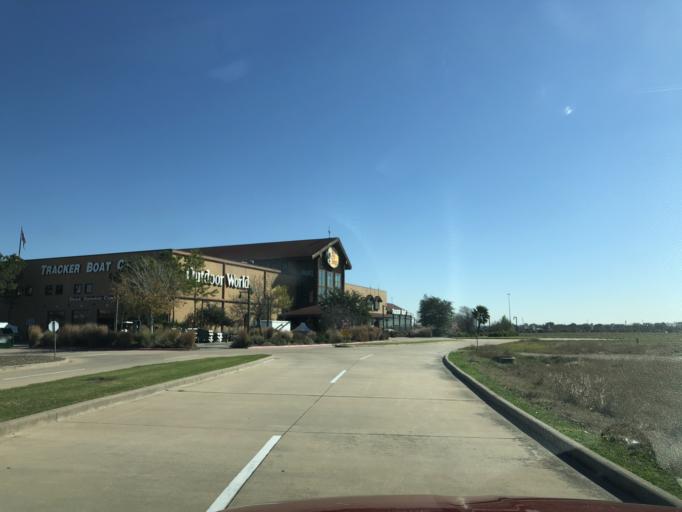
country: US
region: Texas
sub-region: Brazoria County
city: Brookside Village
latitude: 29.5952
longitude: -95.3912
